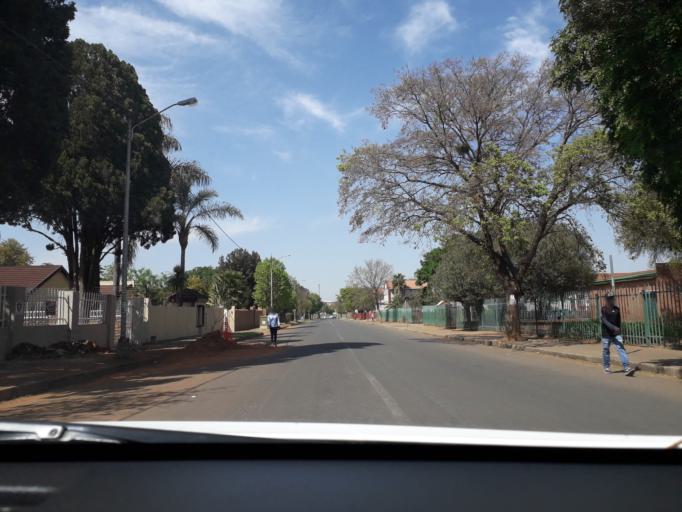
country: ZA
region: Gauteng
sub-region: City of Johannesburg Metropolitan Municipality
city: Modderfontein
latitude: -26.0996
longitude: 28.2375
